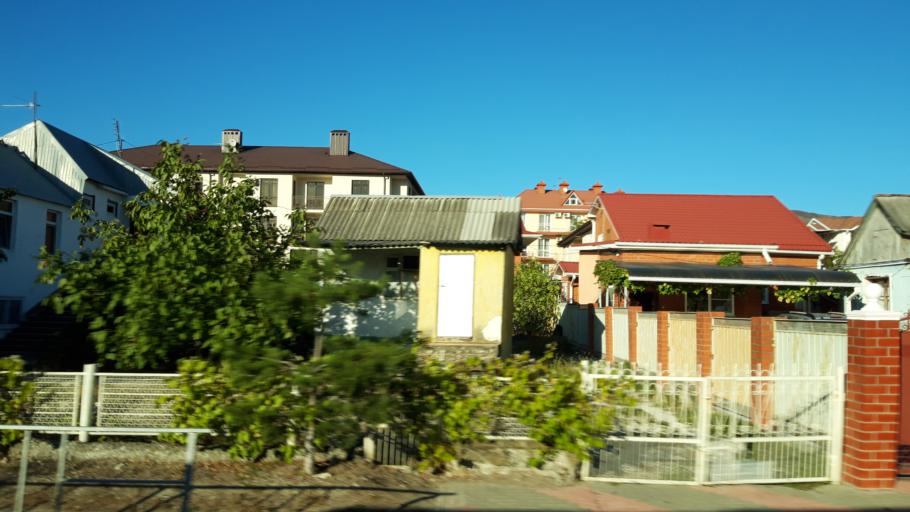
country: RU
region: Krasnodarskiy
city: Kabardinka
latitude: 44.6487
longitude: 37.9475
